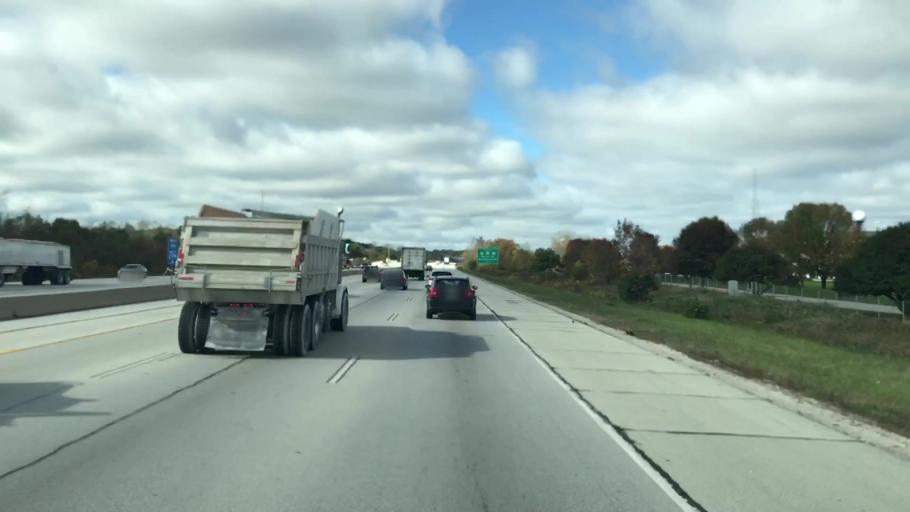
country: US
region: Wisconsin
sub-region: Waukesha County
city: Brookfield
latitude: 43.0291
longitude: -88.1393
